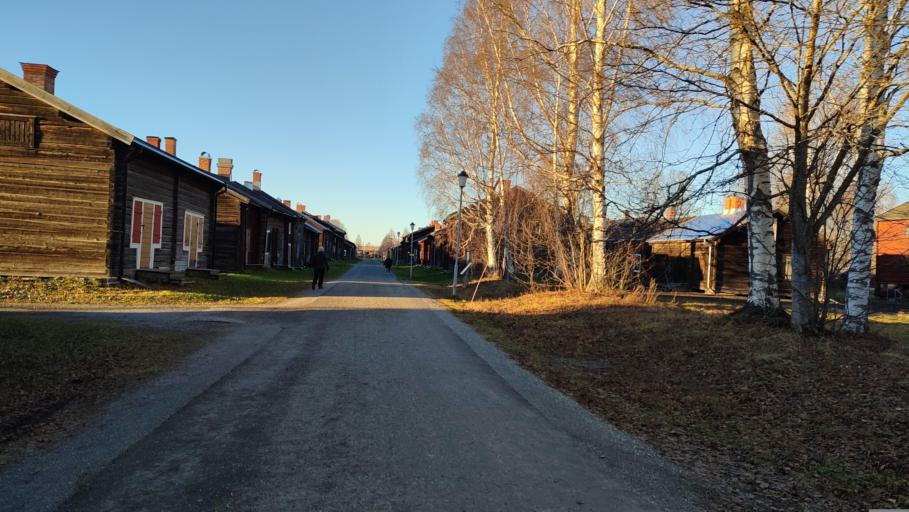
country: SE
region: Vaesterbotten
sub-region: Skelleftea Kommun
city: Skelleftea
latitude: 64.7507
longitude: 20.9323
